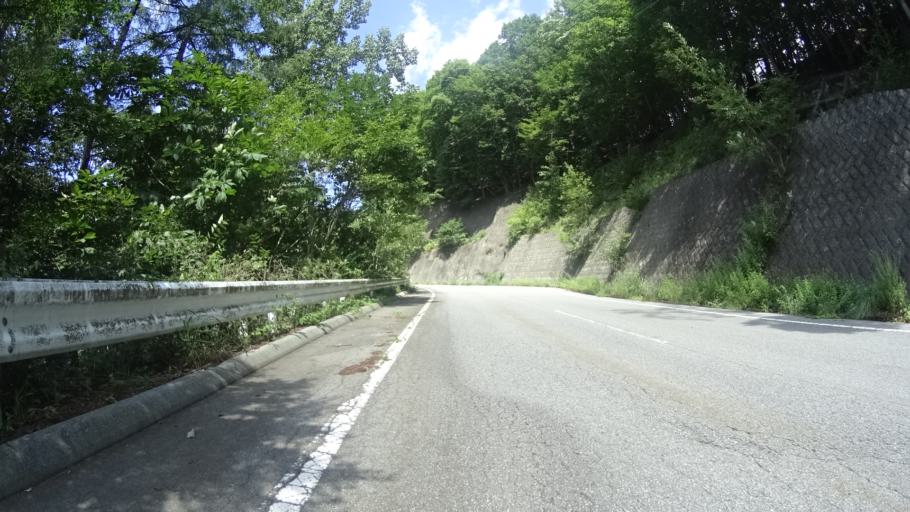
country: JP
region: Yamanashi
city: Enzan
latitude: 35.8026
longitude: 138.6675
